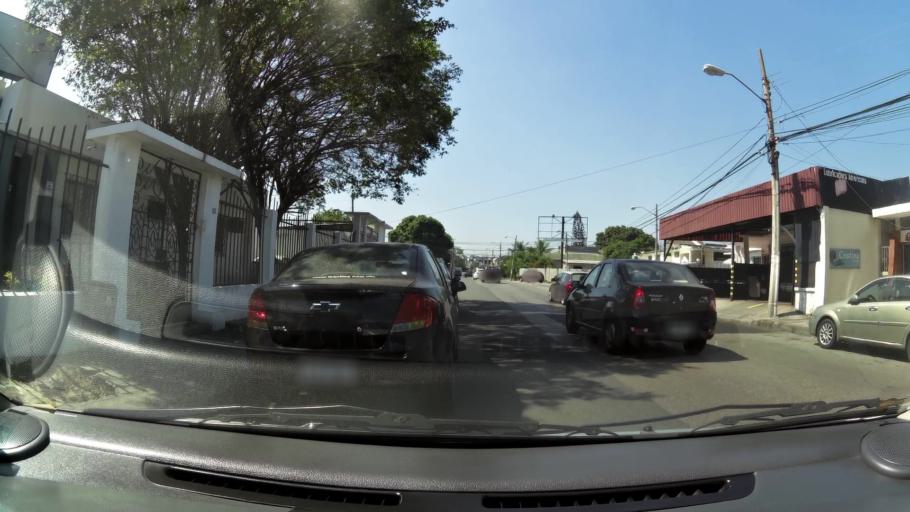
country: EC
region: Guayas
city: Guayaquil
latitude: -2.1661
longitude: -79.9199
